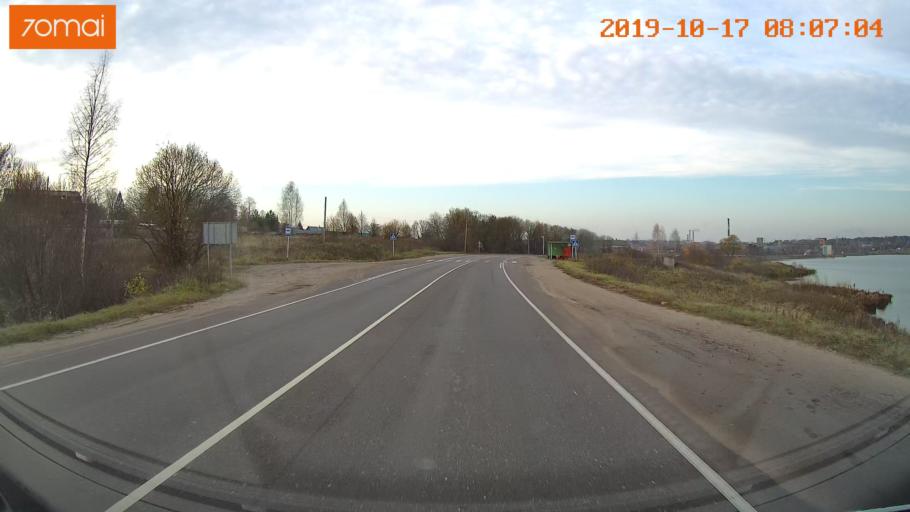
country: RU
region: Vladimir
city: Kol'chugino
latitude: 56.3180
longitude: 39.4027
